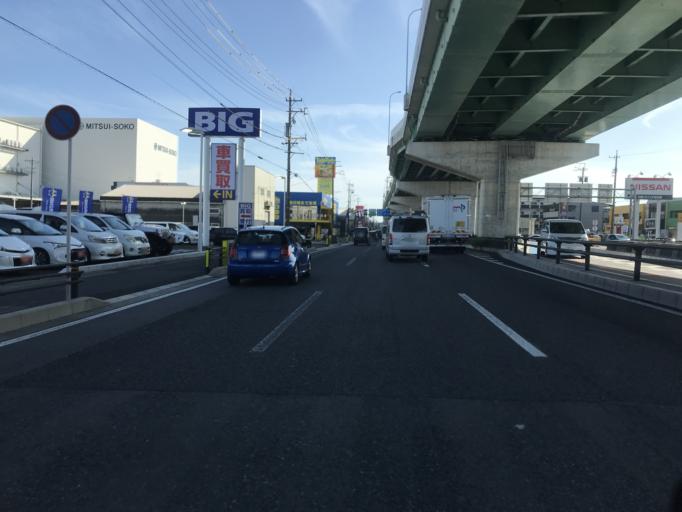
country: JP
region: Aichi
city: Iwakura
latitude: 35.2414
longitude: 136.8469
